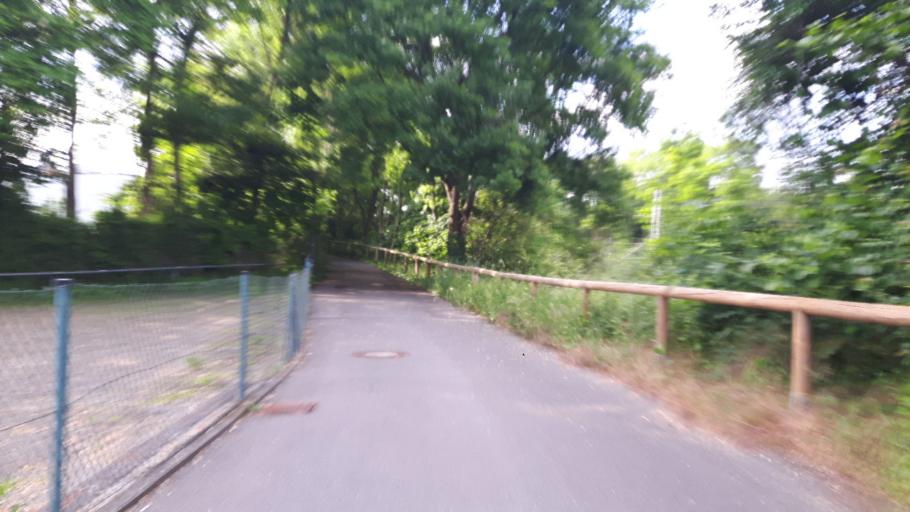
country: DE
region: Bavaria
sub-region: Regierungsbezirk Unterfranken
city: Wuerzburg
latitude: 49.7635
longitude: 9.9413
